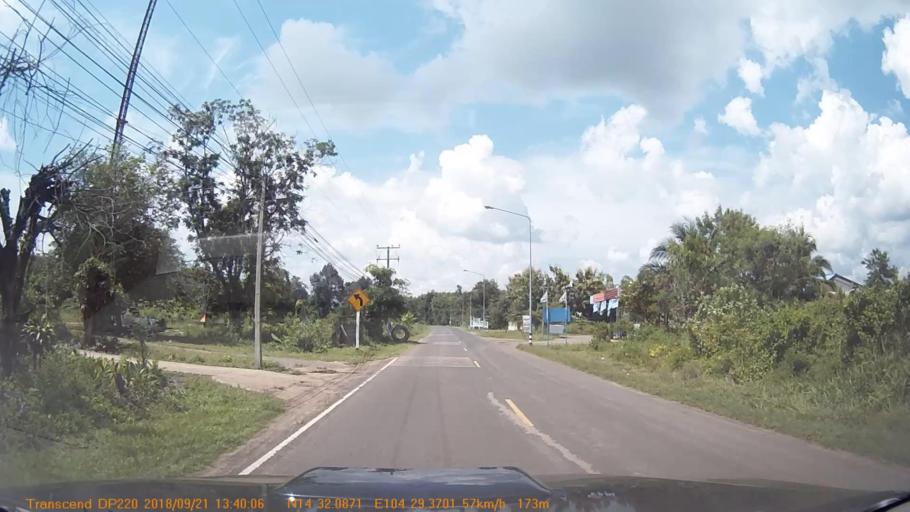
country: TH
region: Sisaket
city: Khun Han
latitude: 14.5352
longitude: 104.4895
